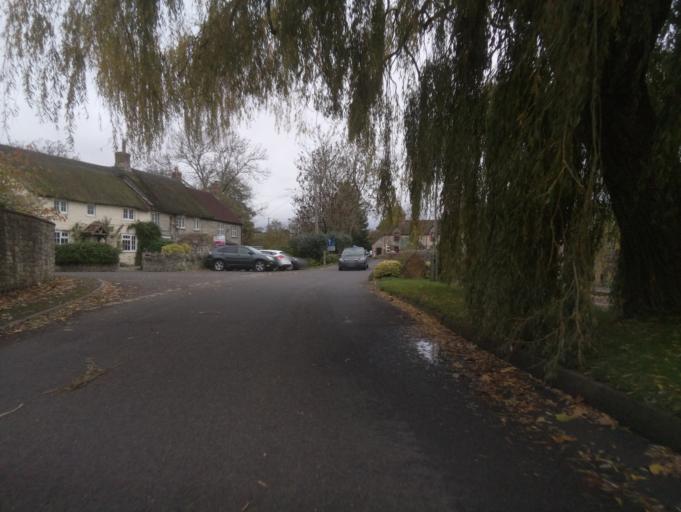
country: GB
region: England
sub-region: Somerset
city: Ilchester
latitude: 51.0197
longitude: -2.6017
